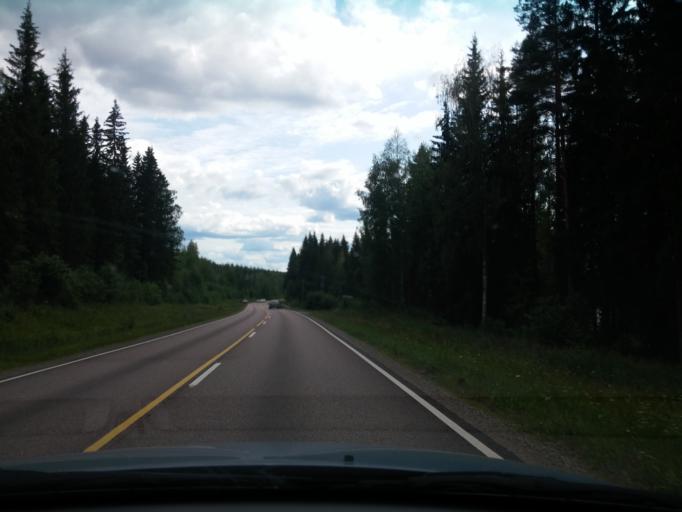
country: FI
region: Central Finland
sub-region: Keuruu
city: Multia
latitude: 62.3709
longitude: 24.7406
